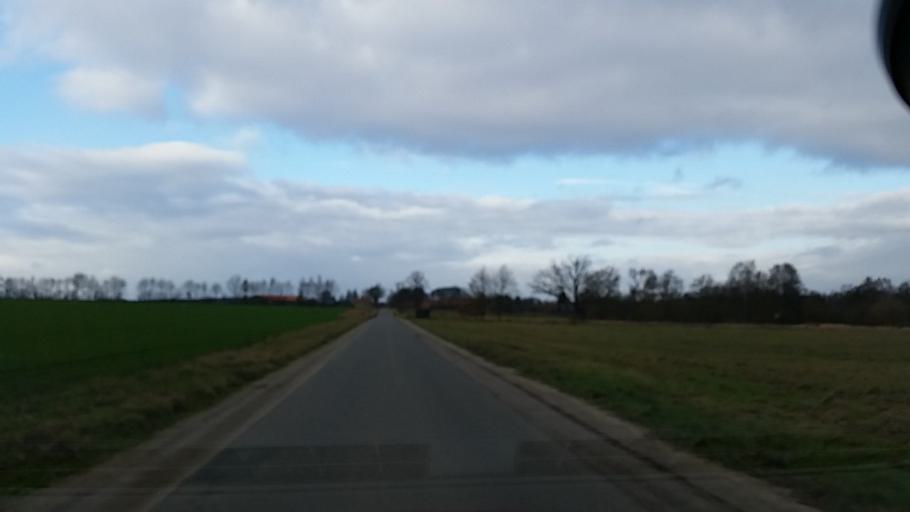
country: DE
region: Lower Saxony
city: Wieren
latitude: 52.8757
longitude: 10.6568
